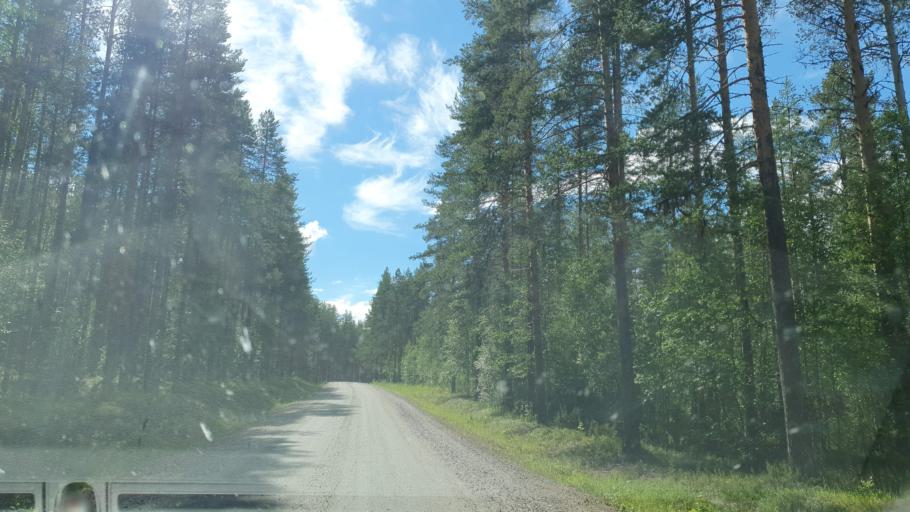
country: FI
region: Kainuu
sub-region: Kehys-Kainuu
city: Kuhmo
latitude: 64.1611
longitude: 29.8235
